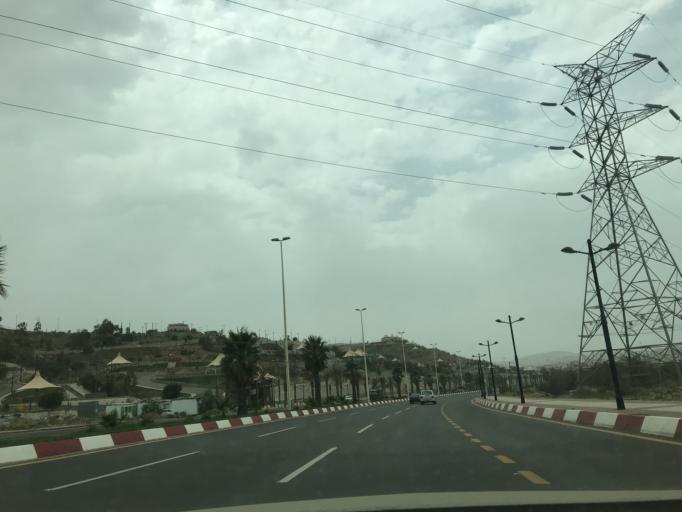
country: SA
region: Mintaqat al Bahah
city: Al Bahah
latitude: 19.8429
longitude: 41.5887
